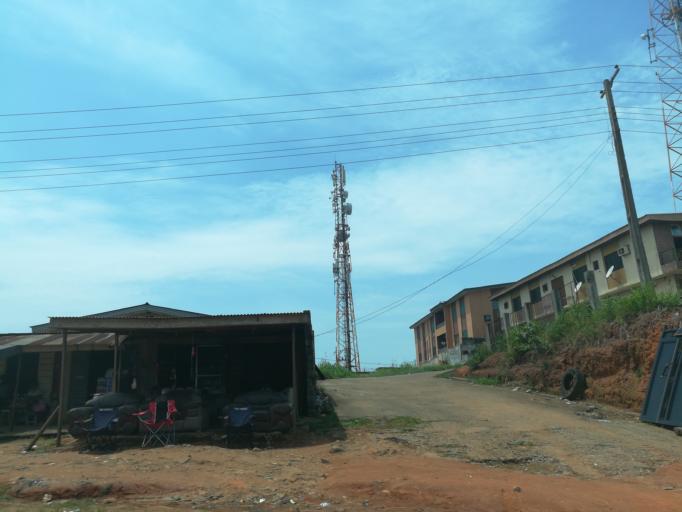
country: NG
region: Lagos
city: Ikorodu
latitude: 6.6248
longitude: 3.4906
